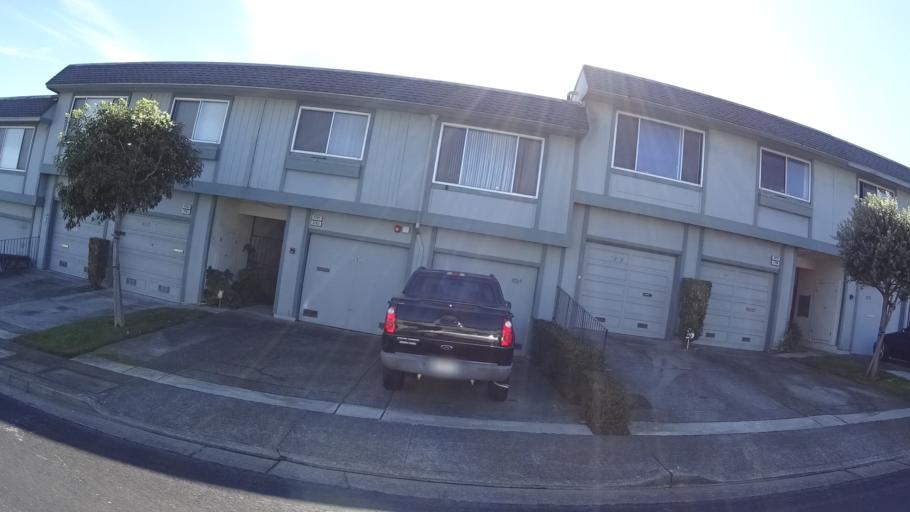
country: US
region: California
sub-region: San Mateo County
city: Colma
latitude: 37.6475
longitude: -122.4591
